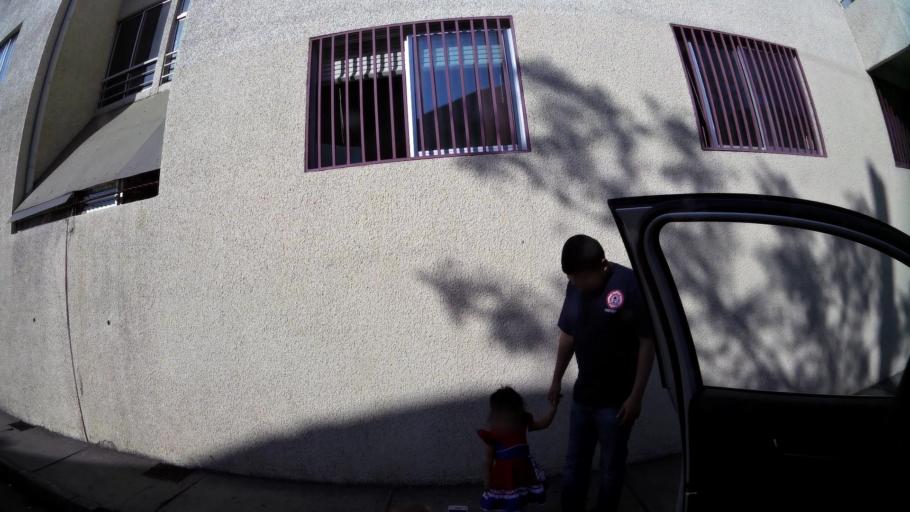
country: CL
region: Santiago Metropolitan
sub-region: Provincia de Santiago
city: Santiago
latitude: -33.4466
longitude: -70.6722
